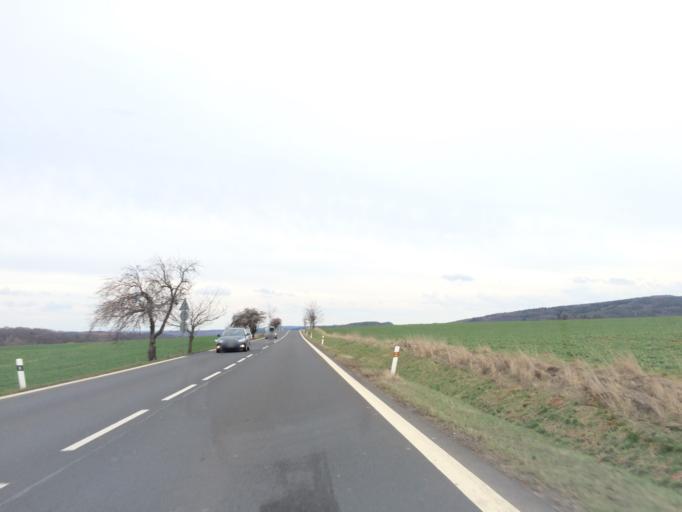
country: CZ
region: Ustecky
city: Lubenec
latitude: 50.1326
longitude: 13.2853
